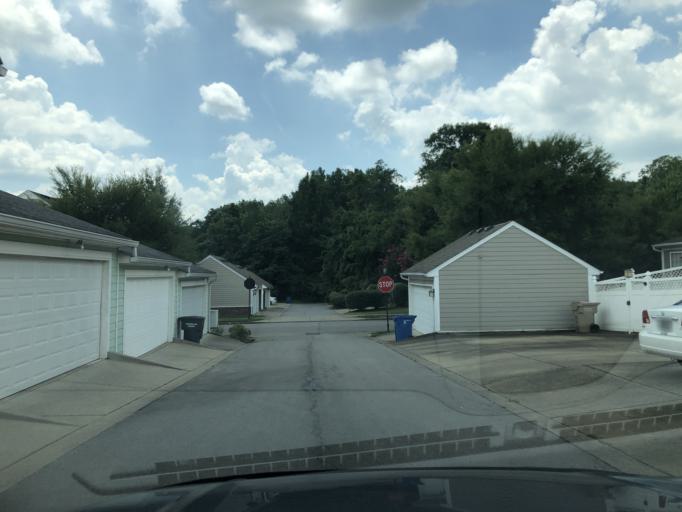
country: US
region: Tennessee
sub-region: Williamson County
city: Brentwood Estates
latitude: 36.0228
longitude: -86.7091
